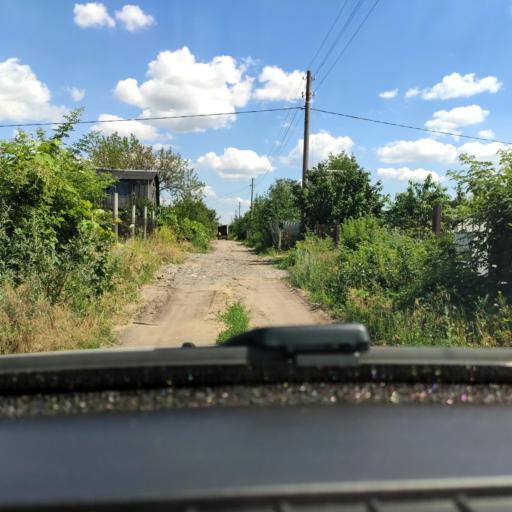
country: RU
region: Voronezj
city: Maslovka
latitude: 51.5045
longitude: 39.2176
